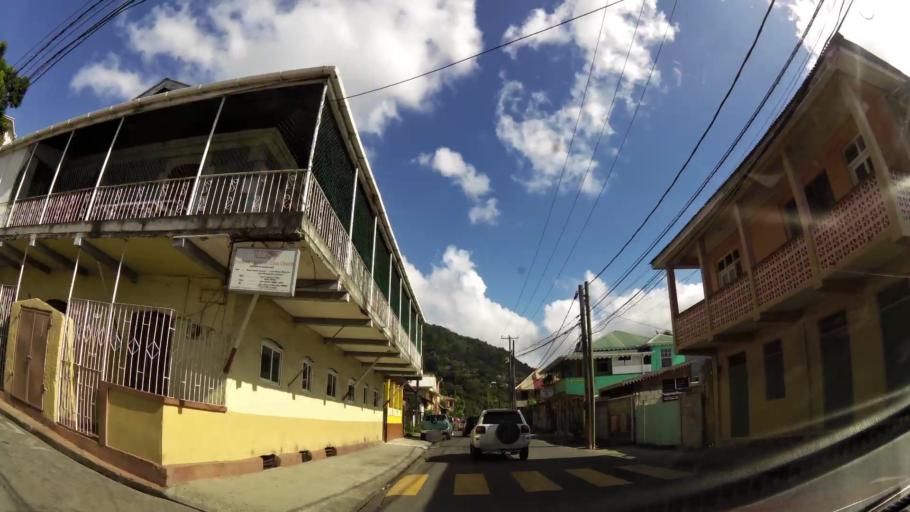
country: DM
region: Saint George
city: Roseau
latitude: 15.2933
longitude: -61.3819
